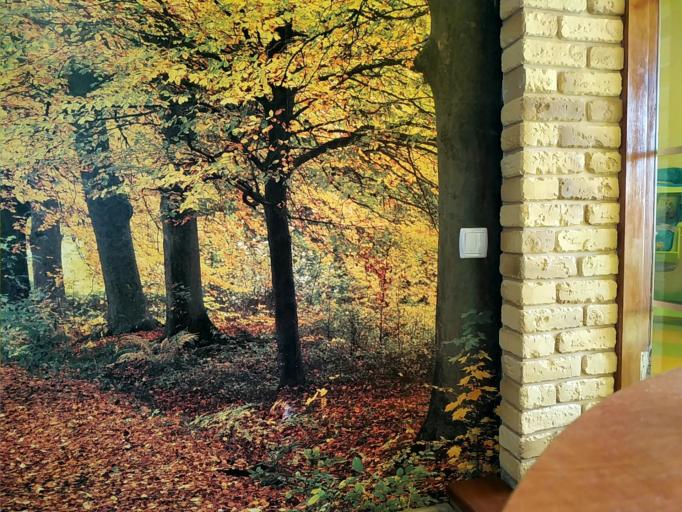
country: RU
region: Novgorod
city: Staraya Russa
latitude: 57.8319
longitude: 31.4873
